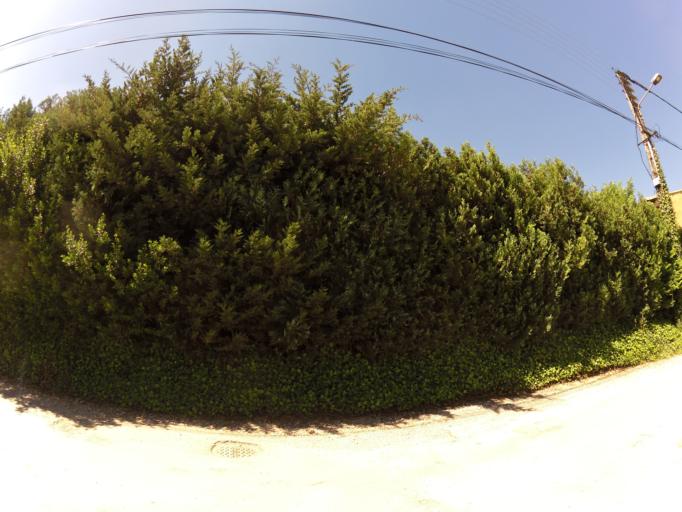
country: FR
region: Languedoc-Roussillon
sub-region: Departement du Gard
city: Mus
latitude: 43.7374
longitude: 4.1958
